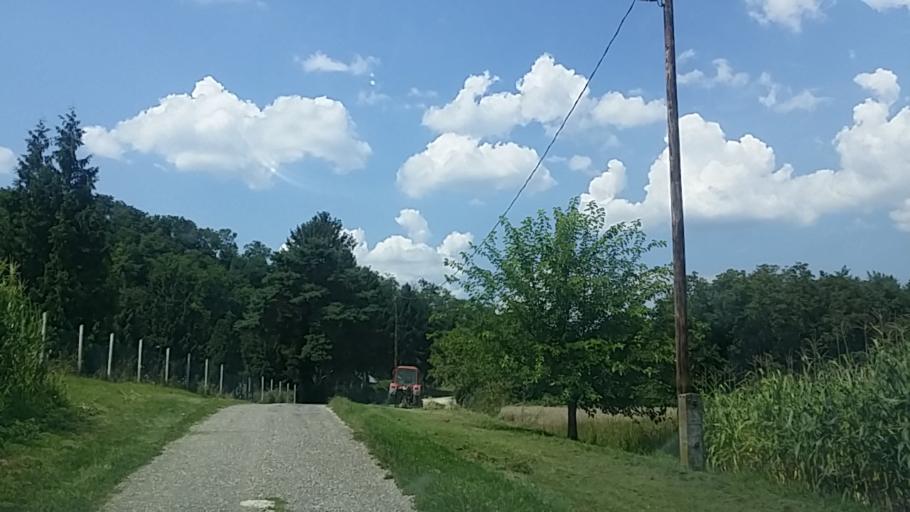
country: HR
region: Medimurska
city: Podturen
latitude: 46.5188
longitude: 16.5503
